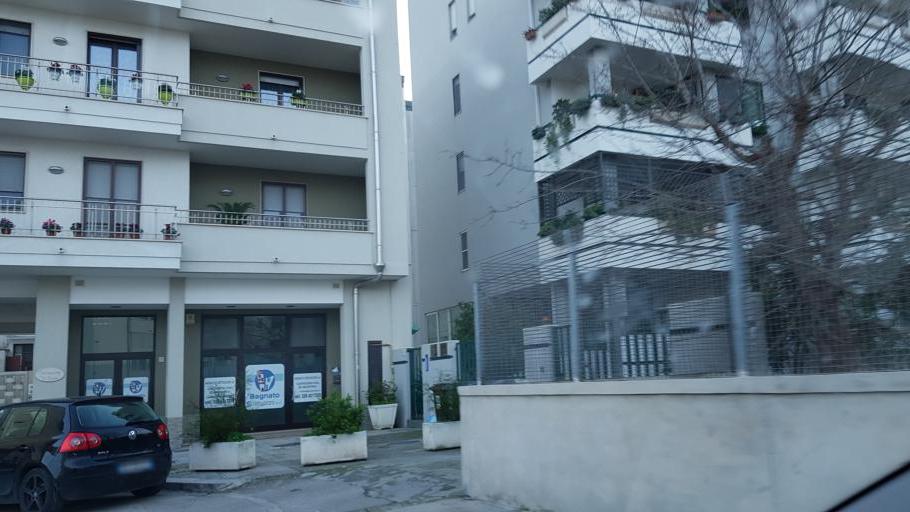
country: IT
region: Apulia
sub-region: Provincia di Brindisi
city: Brindisi
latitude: 40.6370
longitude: 17.9359
